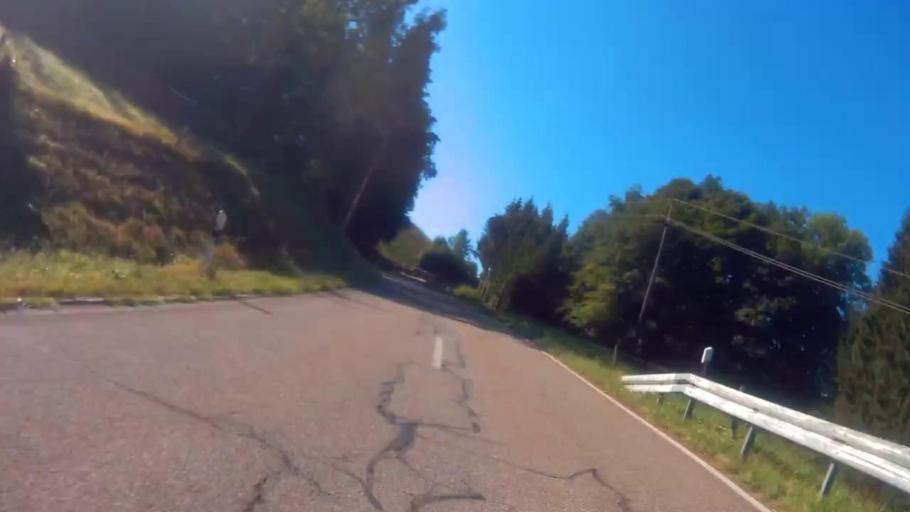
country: DE
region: Baden-Wuerttemberg
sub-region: Freiburg Region
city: Wembach
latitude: 47.7676
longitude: 7.8889
